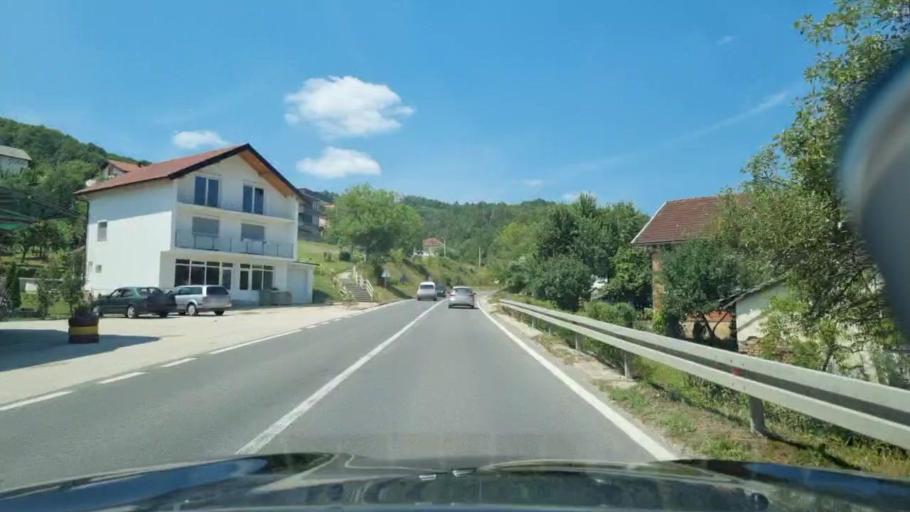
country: BA
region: Federation of Bosnia and Herzegovina
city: Kljuc
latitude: 44.5381
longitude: 16.7612
